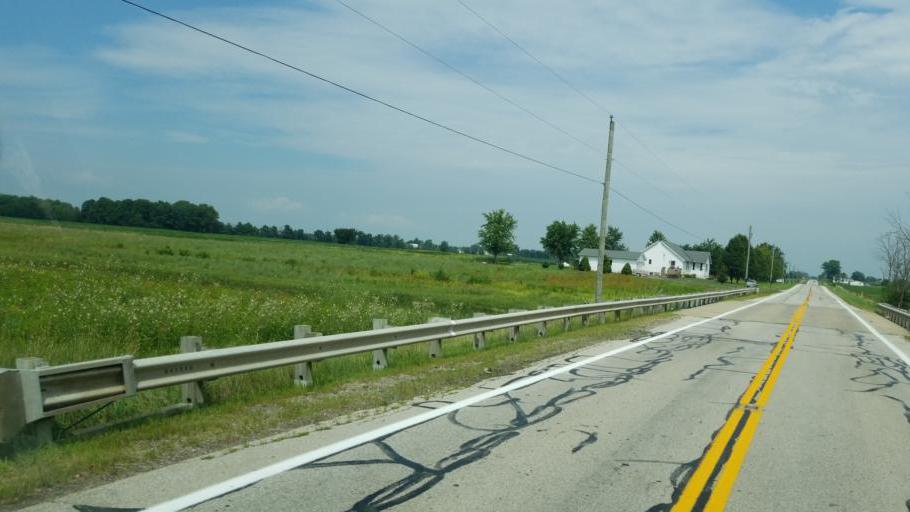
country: US
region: Ohio
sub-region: Union County
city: Marysville
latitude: 40.3460
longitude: -83.3888
